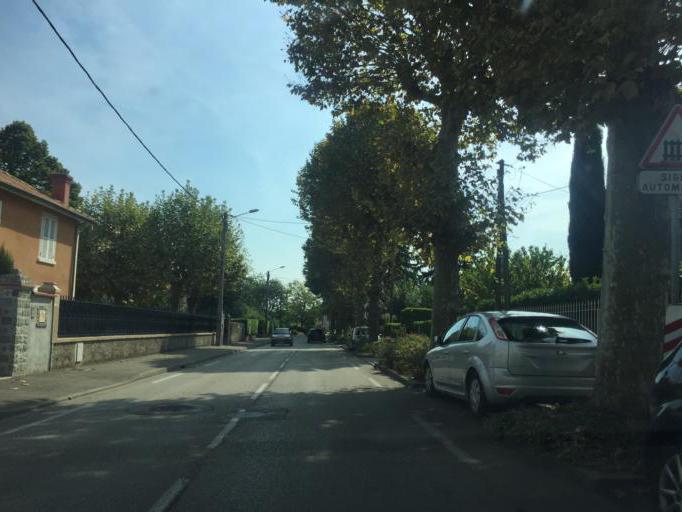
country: FR
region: Rhone-Alpes
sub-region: Departement de l'Ain
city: Beynost
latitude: 45.8352
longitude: 5.0056
